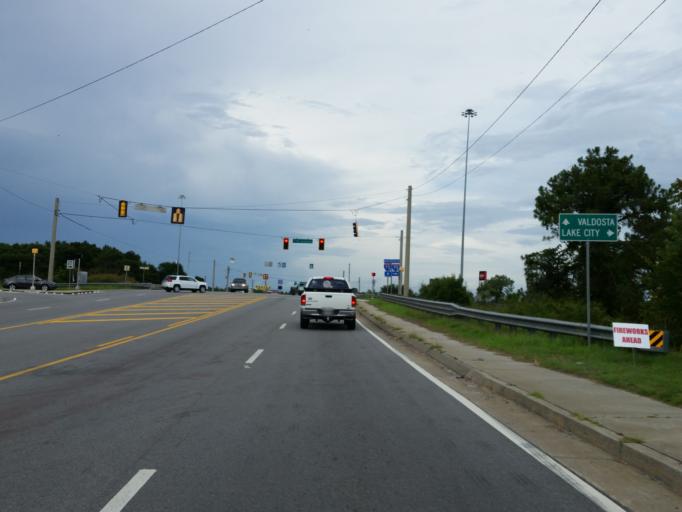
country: US
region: Georgia
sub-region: Lowndes County
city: Valdosta
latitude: 30.6795
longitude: -83.2243
